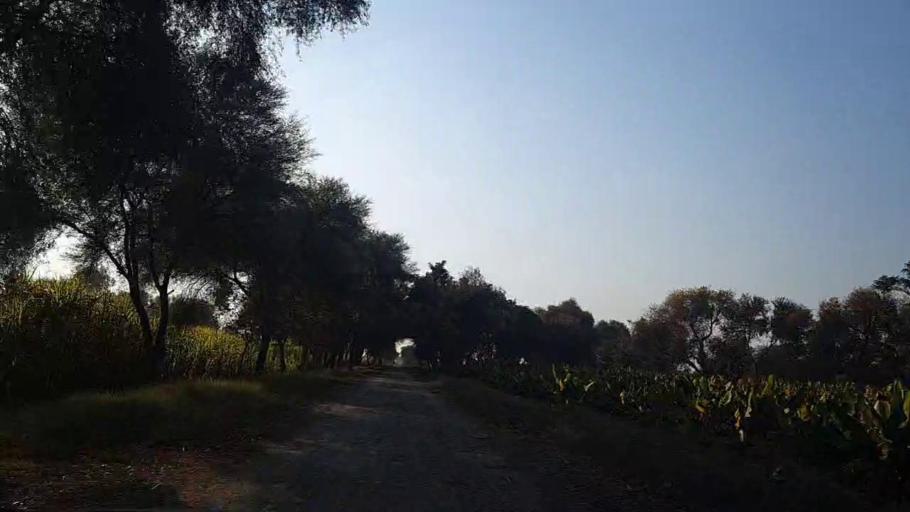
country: PK
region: Sindh
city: Daur
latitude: 26.3331
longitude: 68.1605
